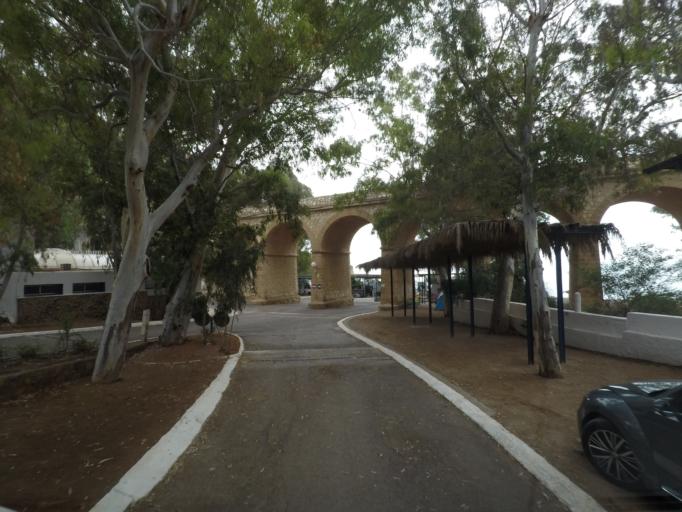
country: ES
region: Andalusia
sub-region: Provincia de Almeria
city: Aguadulce
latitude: 36.8261
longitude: -2.5169
